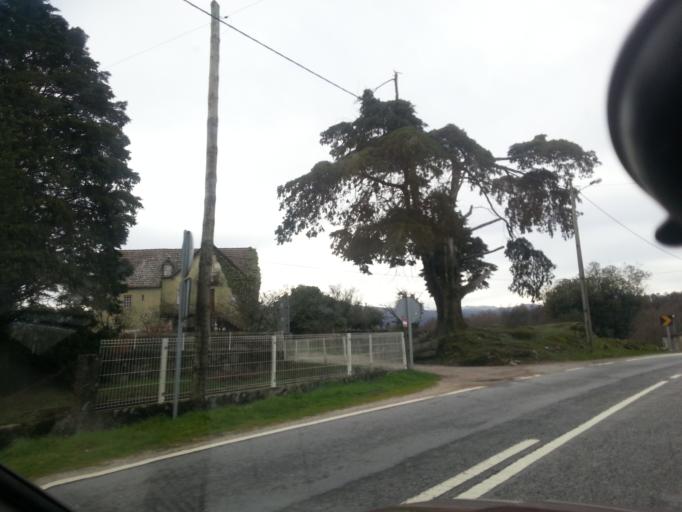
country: PT
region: Guarda
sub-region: Seia
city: Seia
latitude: 40.4901
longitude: -7.6588
